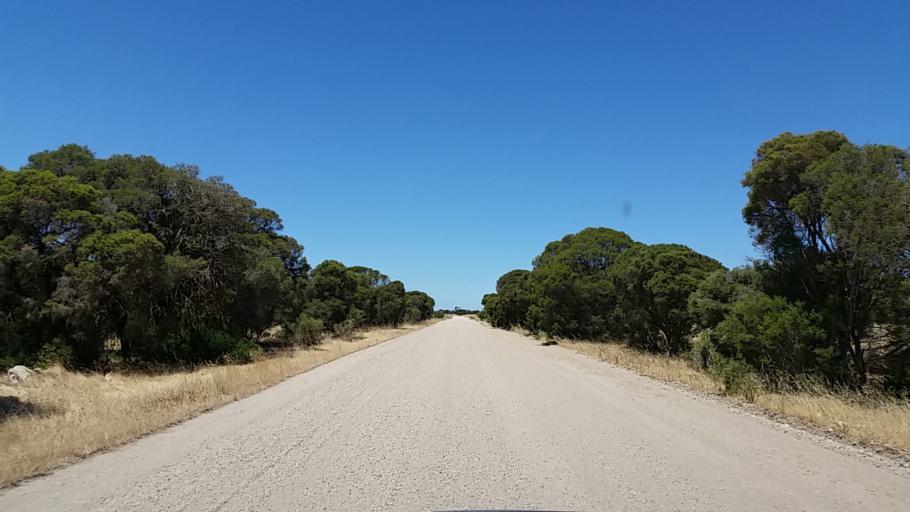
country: AU
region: South Australia
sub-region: Yorke Peninsula
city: Honiton
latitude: -35.0805
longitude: 137.4808
